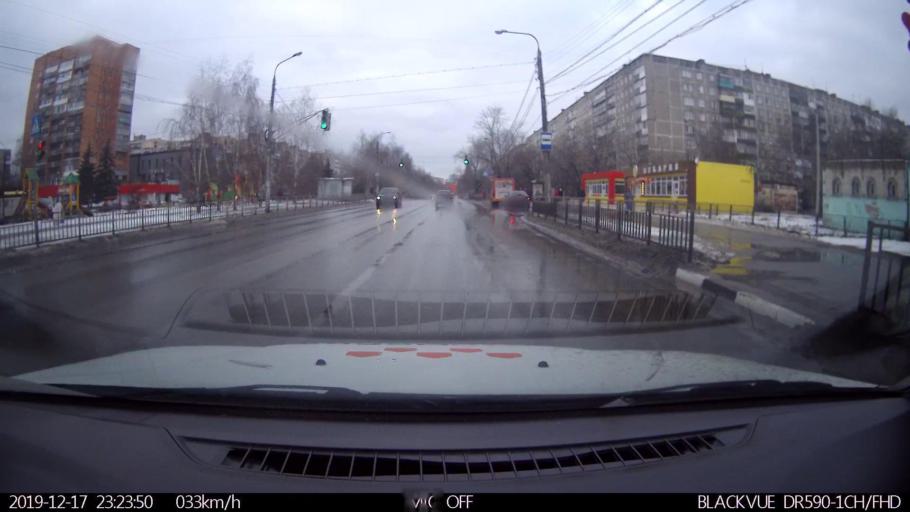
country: RU
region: Nizjnij Novgorod
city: Gorbatovka
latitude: 56.3596
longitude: 43.8234
